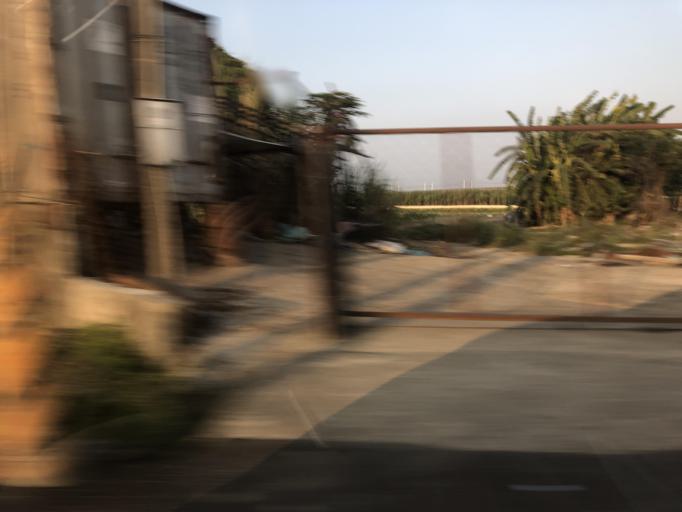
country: TW
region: Taiwan
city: Xinying
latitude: 23.1573
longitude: 120.2743
